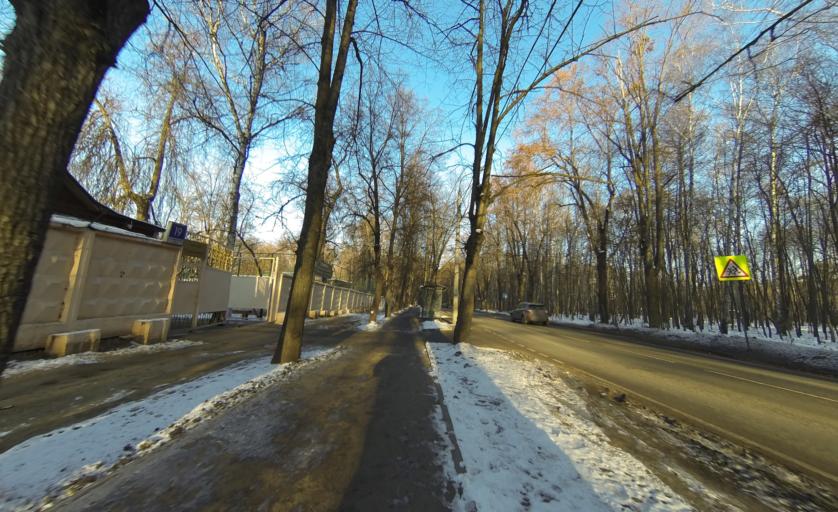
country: RU
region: Moscow
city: Sokol'niki
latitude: 55.8103
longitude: 37.6827
